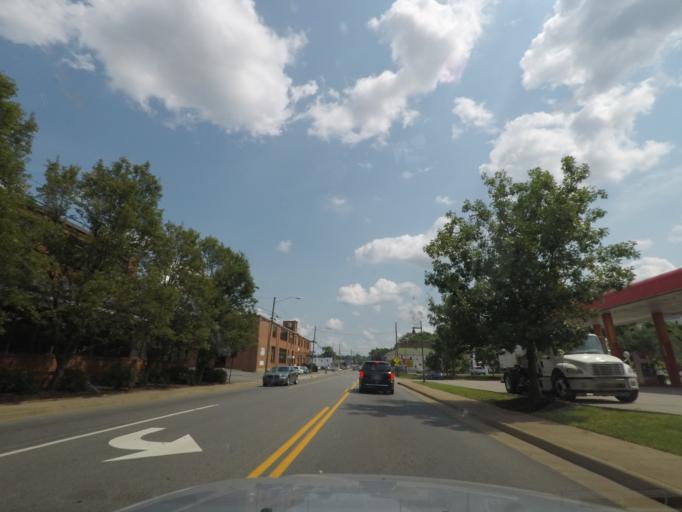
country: US
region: Virginia
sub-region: Orange County
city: Orange
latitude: 38.2526
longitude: -78.1146
